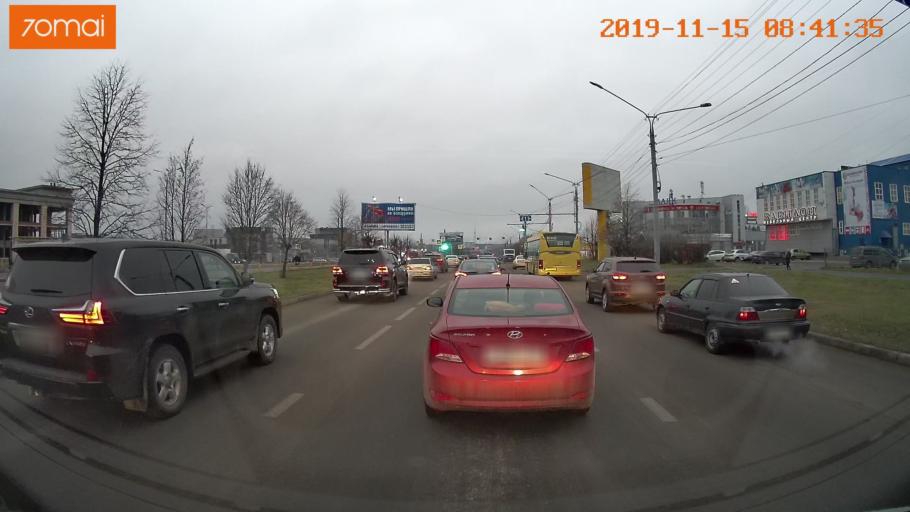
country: RU
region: Vologda
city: Cherepovets
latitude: 59.0975
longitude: 37.9118
